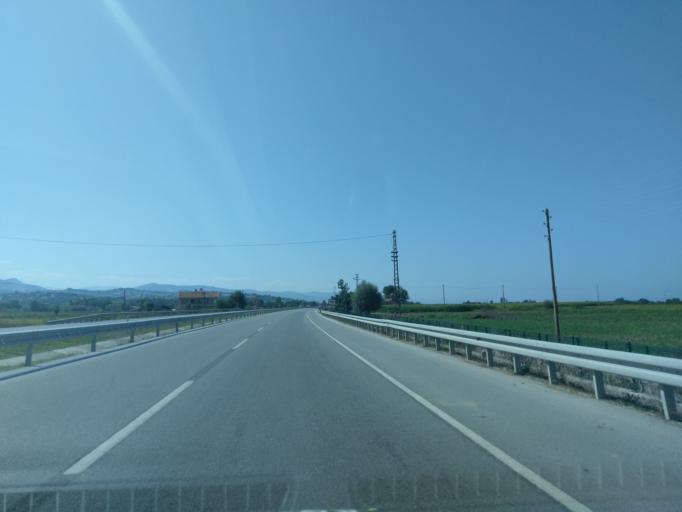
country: TR
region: Samsun
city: Alacam
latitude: 41.6085
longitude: 35.6663
